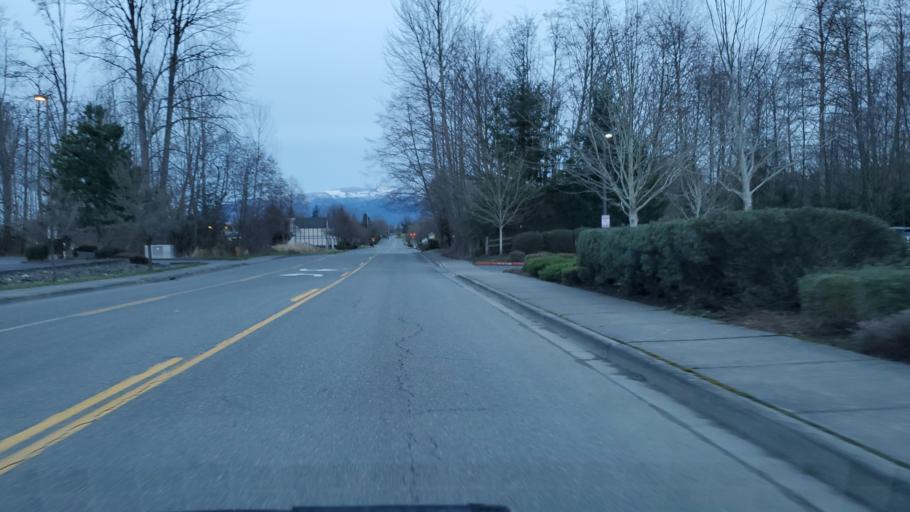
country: US
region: Washington
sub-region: Skagit County
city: Mount Vernon
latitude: 48.4339
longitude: -122.3252
